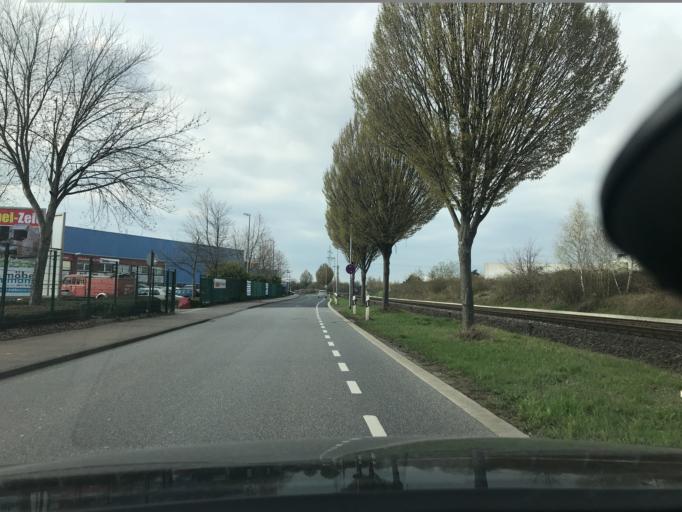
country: DE
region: North Rhine-Westphalia
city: Kempen
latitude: 51.3751
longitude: 6.4198
